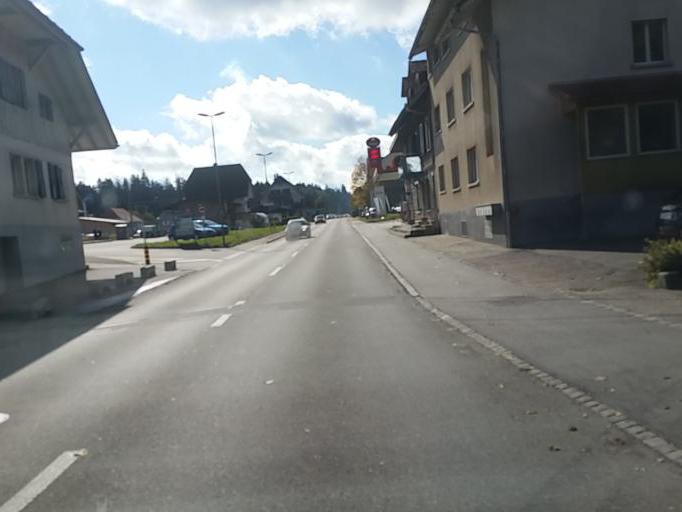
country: CH
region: Bern
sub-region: Emmental District
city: Sumiswald
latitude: 47.0631
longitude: 7.7493
